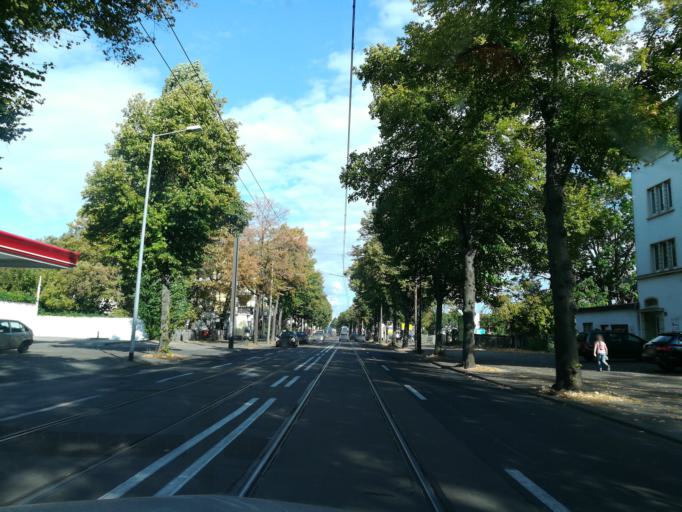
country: DE
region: Saxony-Anhalt
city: Diesdorf
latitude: 52.1289
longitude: 11.5965
